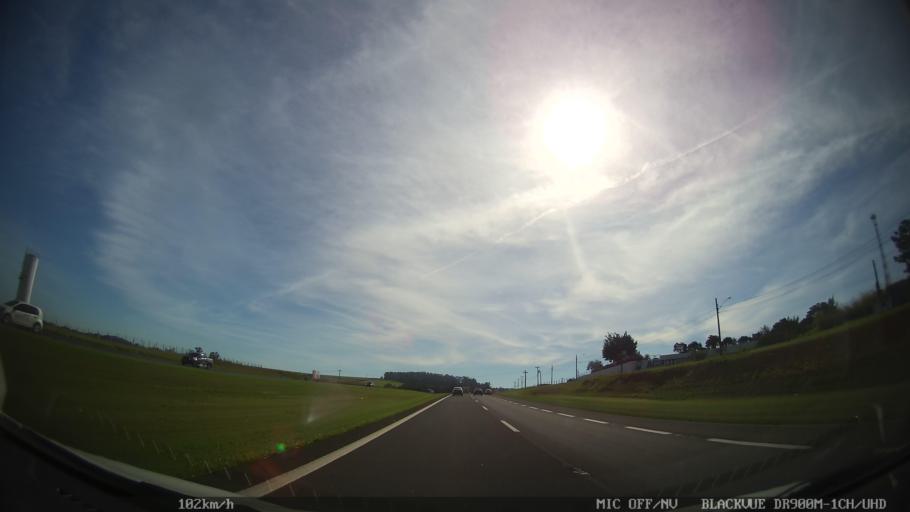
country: BR
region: Sao Paulo
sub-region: Araras
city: Araras
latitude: -22.3467
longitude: -47.3939
